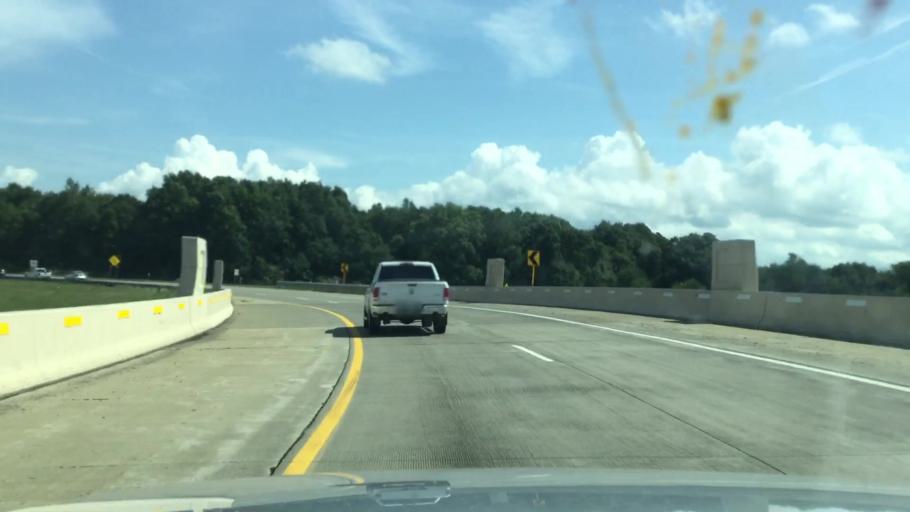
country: US
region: Michigan
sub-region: Kalamazoo County
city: Westwood
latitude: 42.2357
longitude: -85.6381
